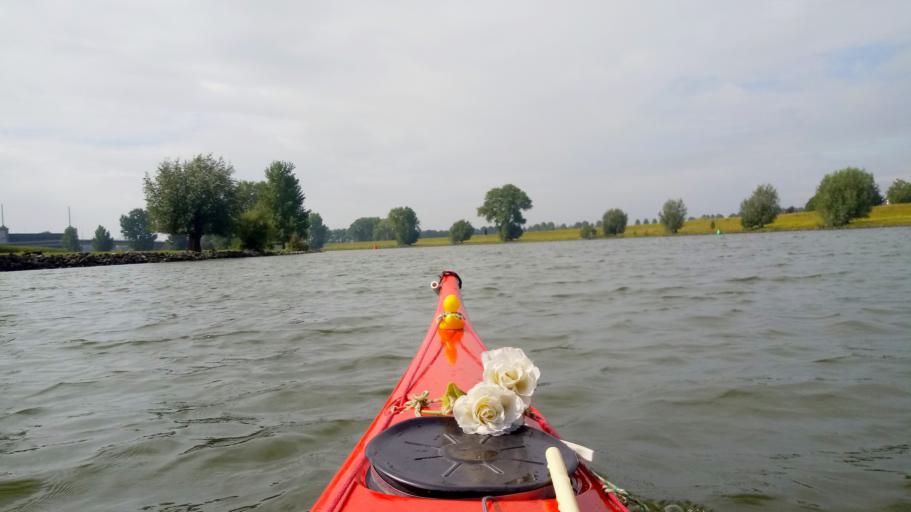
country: NL
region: North Brabant
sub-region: Gemeente Aalburg
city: Aalburg
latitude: 51.7465
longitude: 5.1298
